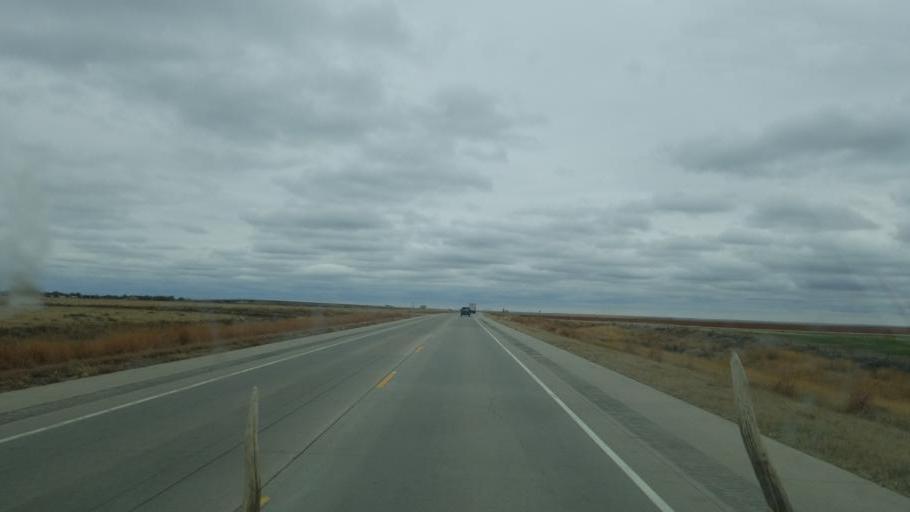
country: US
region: Colorado
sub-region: Kiowa County
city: Eads
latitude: 38.7483
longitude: -102.7768
